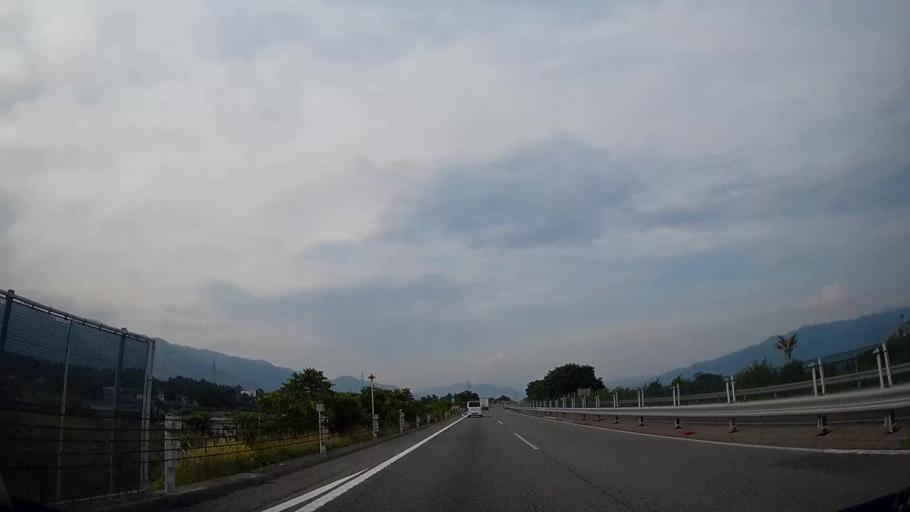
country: JP
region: Nagano
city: Ina
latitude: 35.9085
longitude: 137.9644
